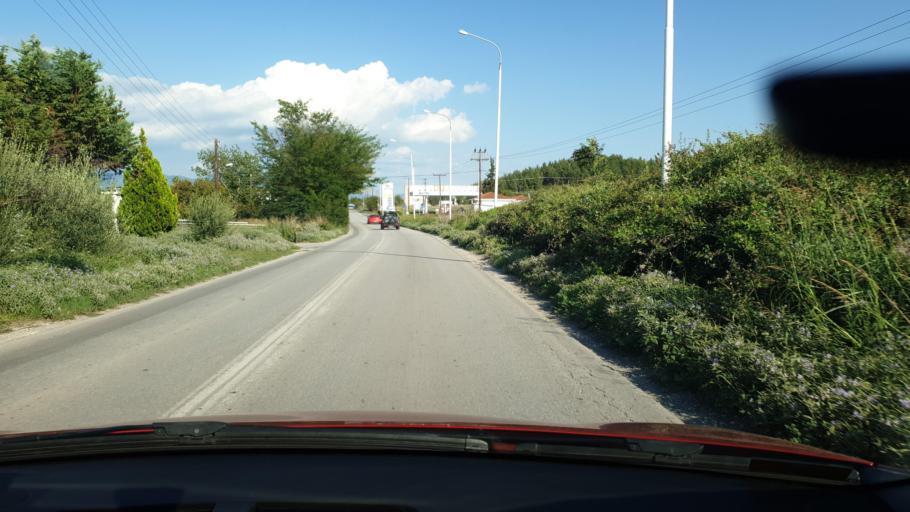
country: GR
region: Central Macedonia
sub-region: Nomos Thessalonikis
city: Neo Rysi
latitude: 40.4949
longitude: 23.0076
